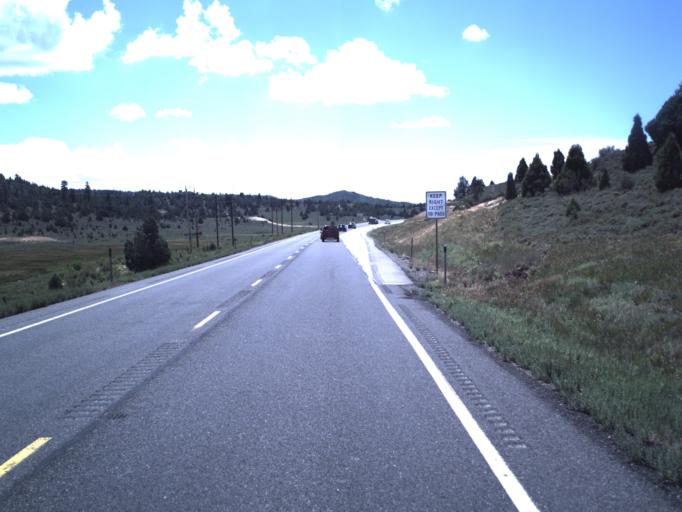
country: US
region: Utah
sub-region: Garfield County
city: Panguitch
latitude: 37.5120
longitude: -112.4977
